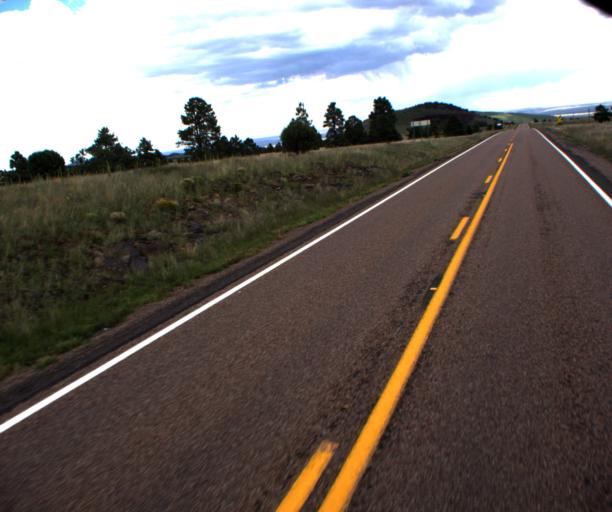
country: US
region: Arizona
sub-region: Apache County
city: Eagar
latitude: 34.0835
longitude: -109.4473
